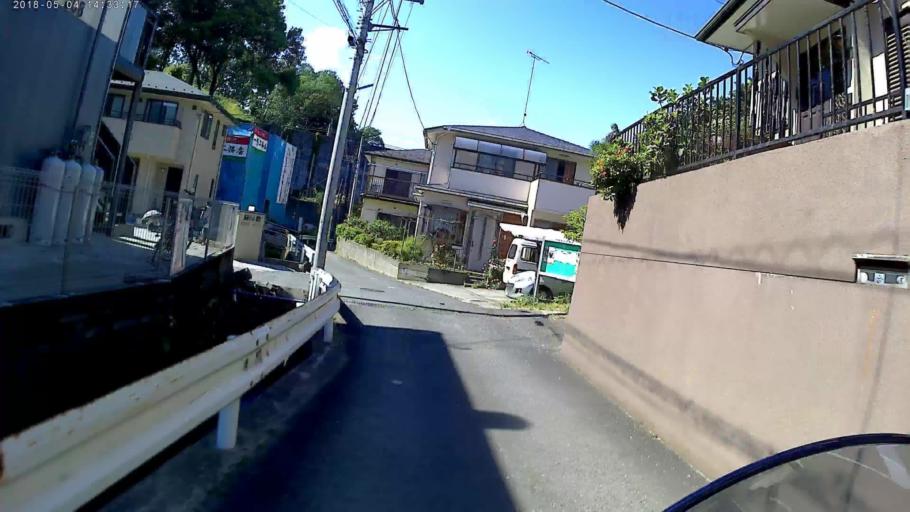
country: JP
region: Kanagawa
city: Yokohama
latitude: 35.4888
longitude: 139.5995
